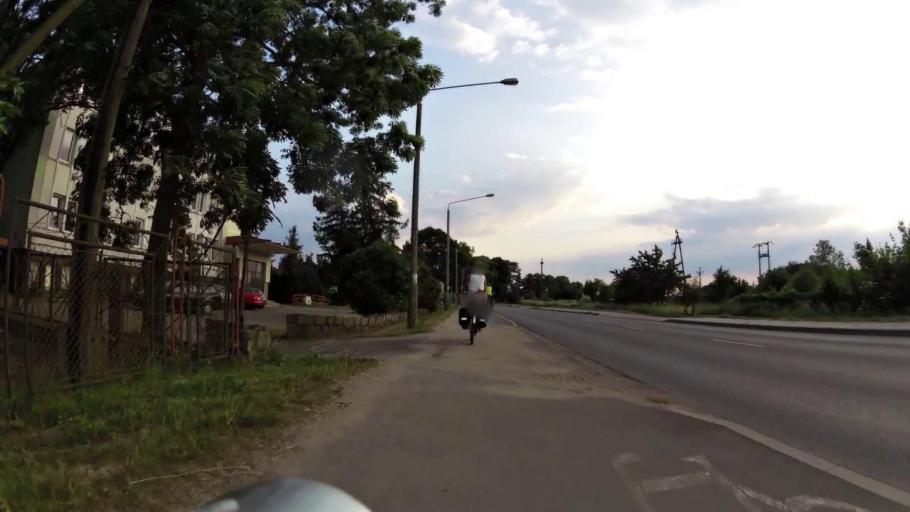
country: PL
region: Kujawsko-Pomorskie
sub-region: Powiat chelminski
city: Unislaw
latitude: 53.2024
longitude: 18.3730
